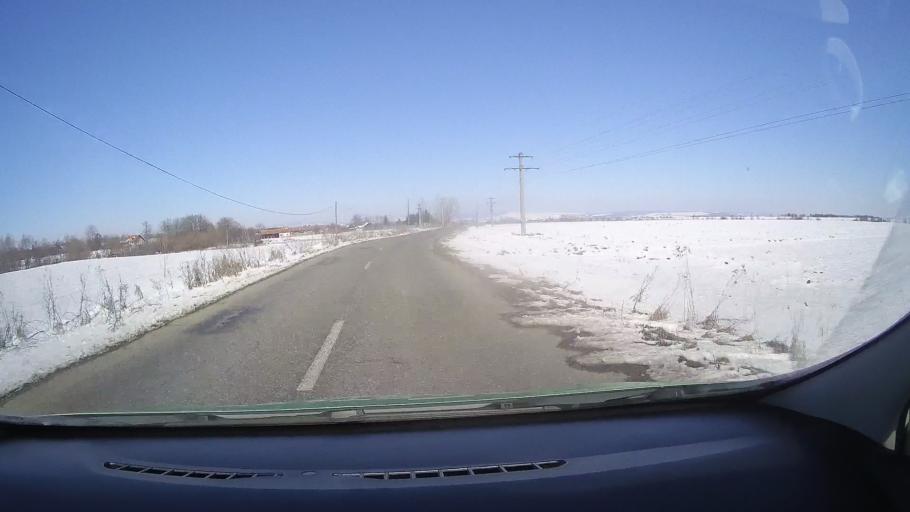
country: RO
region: Brasov
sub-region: Comuna Harseni
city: Harseni
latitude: 45.7779
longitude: 25.0010
